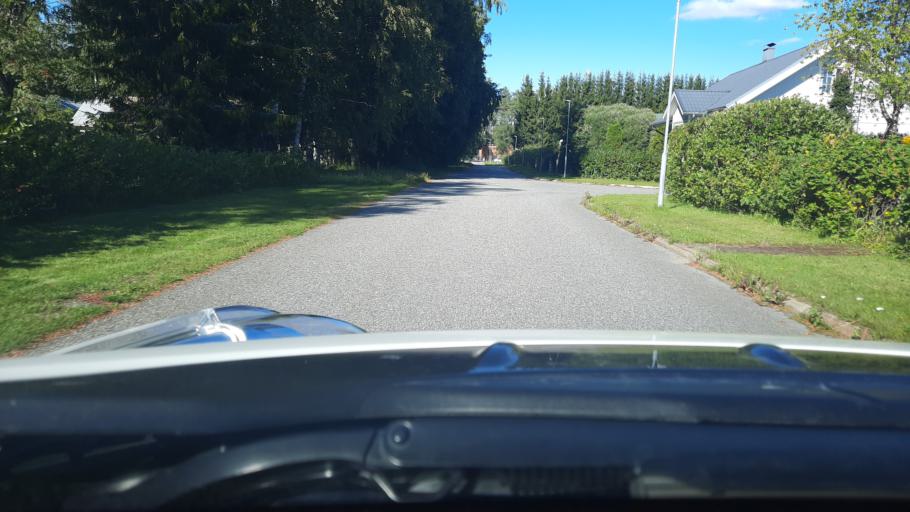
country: FI
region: North Karelia
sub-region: Joensuu
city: Joensuu
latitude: 62.6362
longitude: 29.6847
